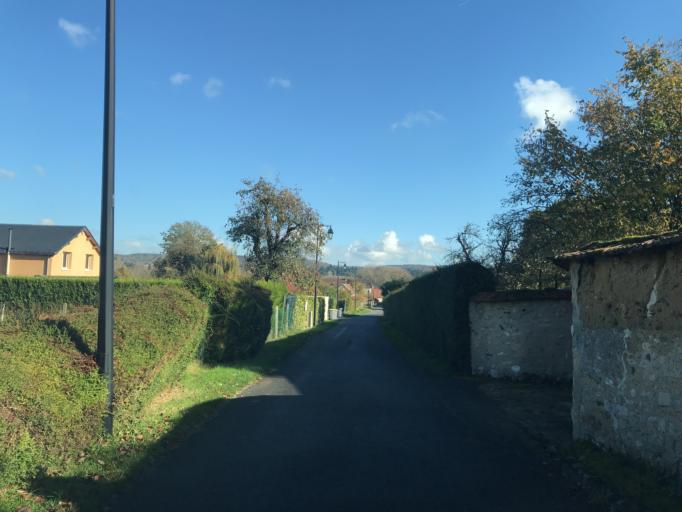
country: FR
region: Haute-Normandie
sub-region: Departement de l'Eure
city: Saint-Just
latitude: 49.1216
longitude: 1.4326
